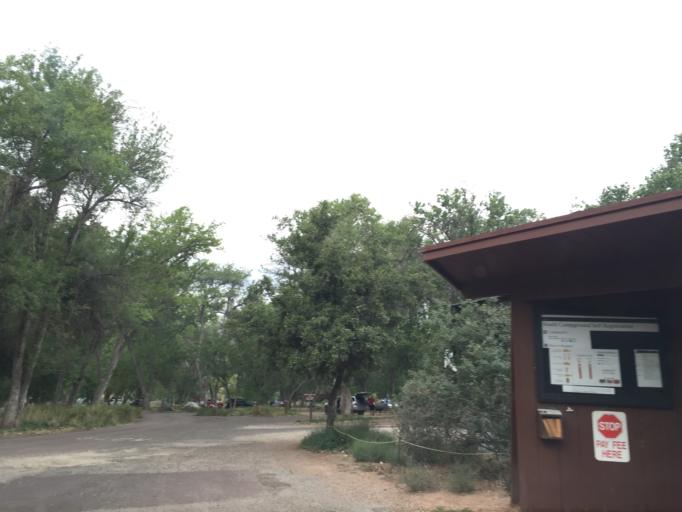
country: US
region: Utah
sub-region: Washington County
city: Hildale
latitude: 37.2039
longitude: -112.9841
